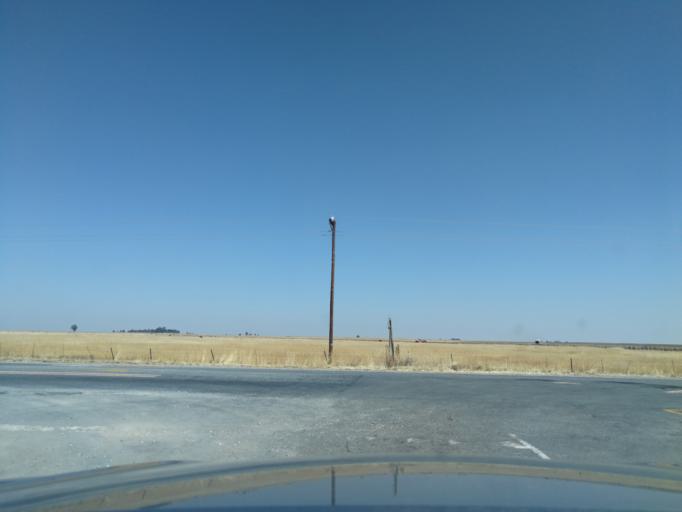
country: ZA
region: North-West
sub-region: Dr Kenneth Kaunda District Municipality
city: Orkney
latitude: -27.0524
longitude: 26.7154
